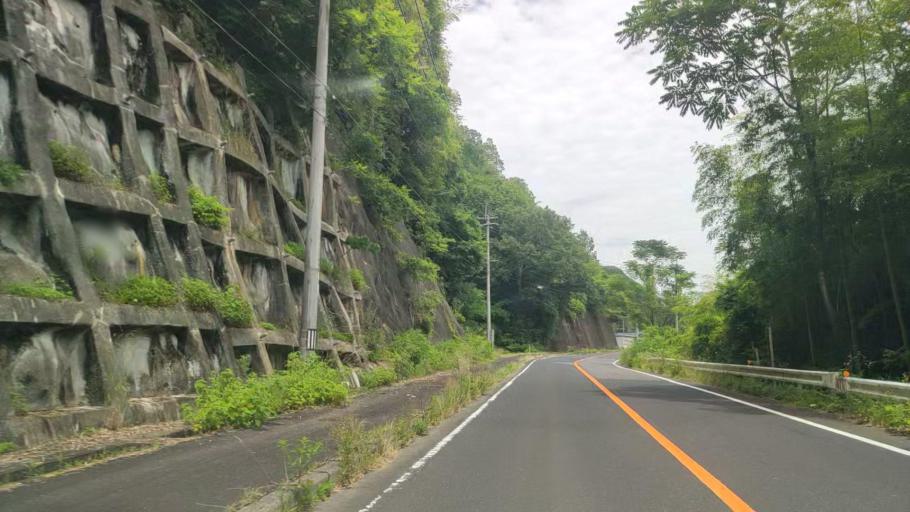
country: JP
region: Okayama
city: Tsuyama
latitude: 35.0900
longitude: 134.2588
